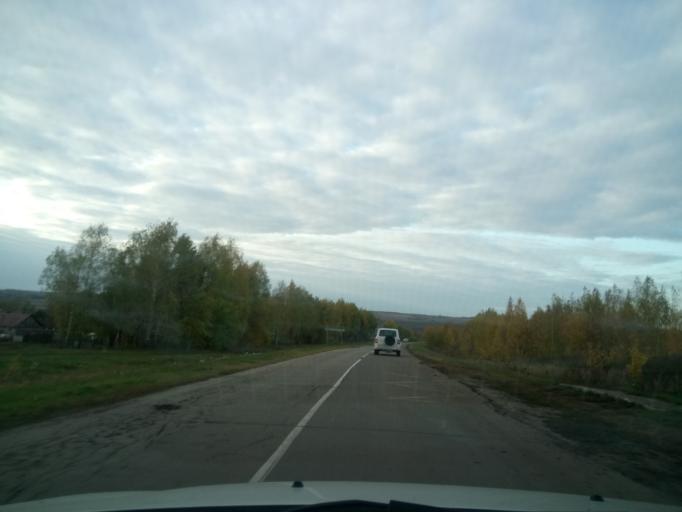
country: RU
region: Nizjnij Novgorod
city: Gagino
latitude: 55.3717
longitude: 45.0896
